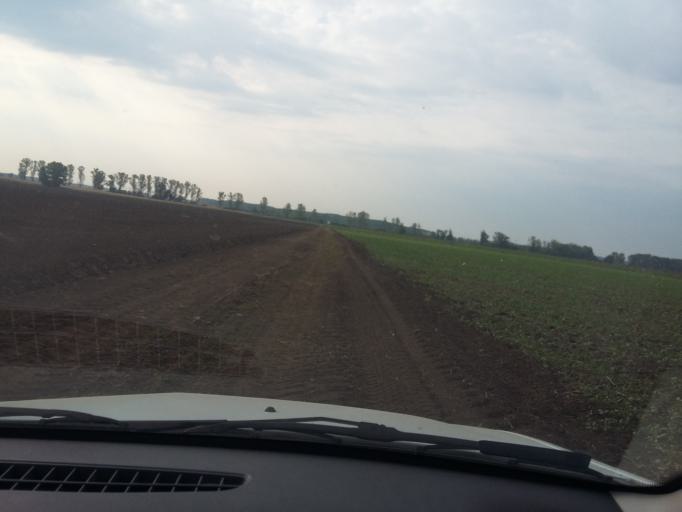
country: HU
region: Borsod-Abauj-Zemplen
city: Taktaharkany
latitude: 48.1241
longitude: 21.1074
